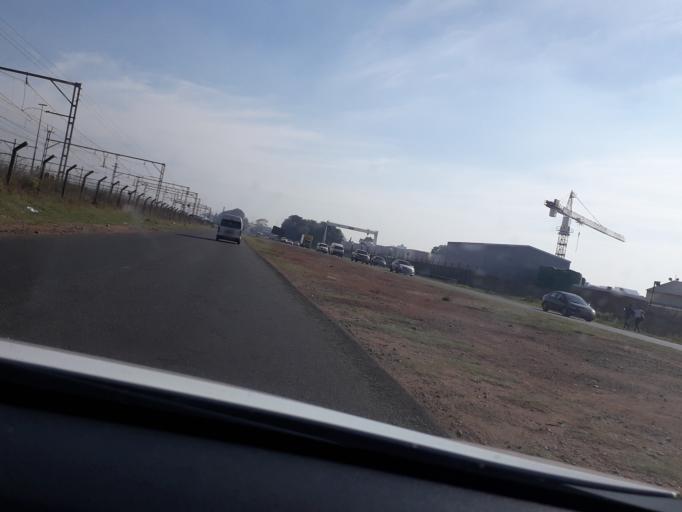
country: ZA
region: Gauteng
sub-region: Ekurhuleni Metropolitan Municipality
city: Boksburg
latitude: -26.1517
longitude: 28.2154
